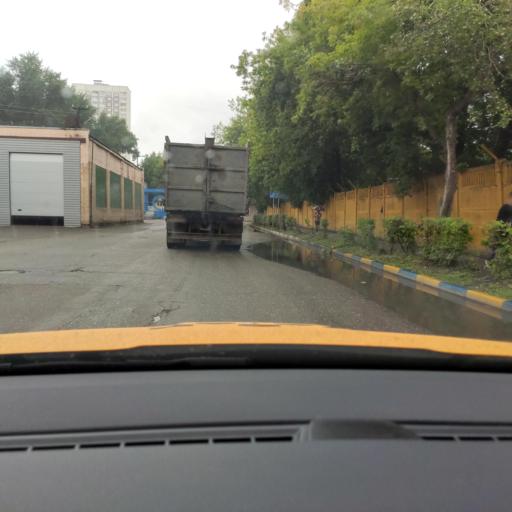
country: RU
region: Moskovskaya
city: Kozhukhovo
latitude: 55.7004
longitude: 37.6906
